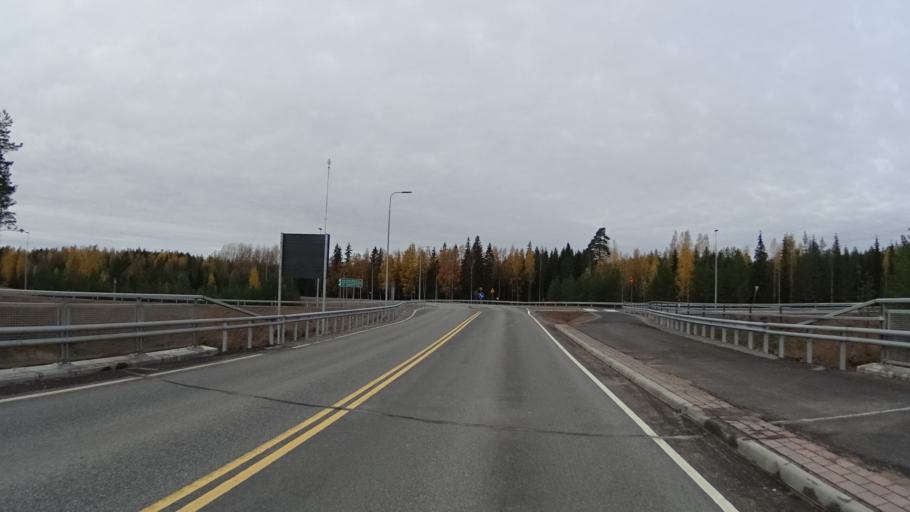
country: FI
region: South Karelia
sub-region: Lappeenranta
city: Lemi
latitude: 60.9759
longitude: 27.8711
